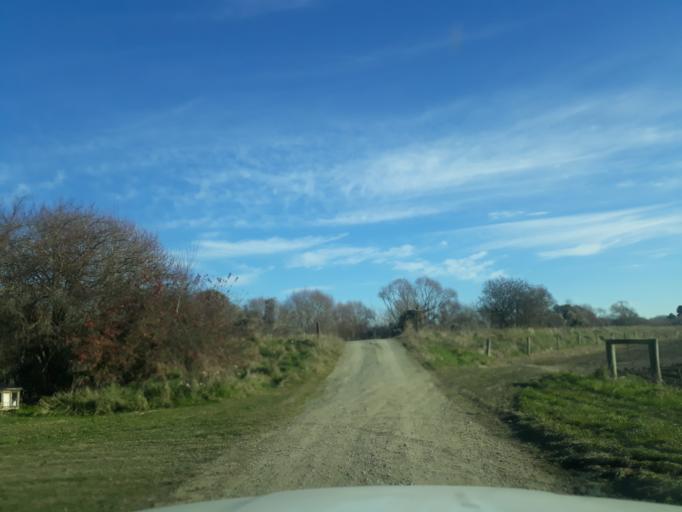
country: NZ
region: Canterbury
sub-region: Timaru District
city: Timaru
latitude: -44.2697
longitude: 171.3330
